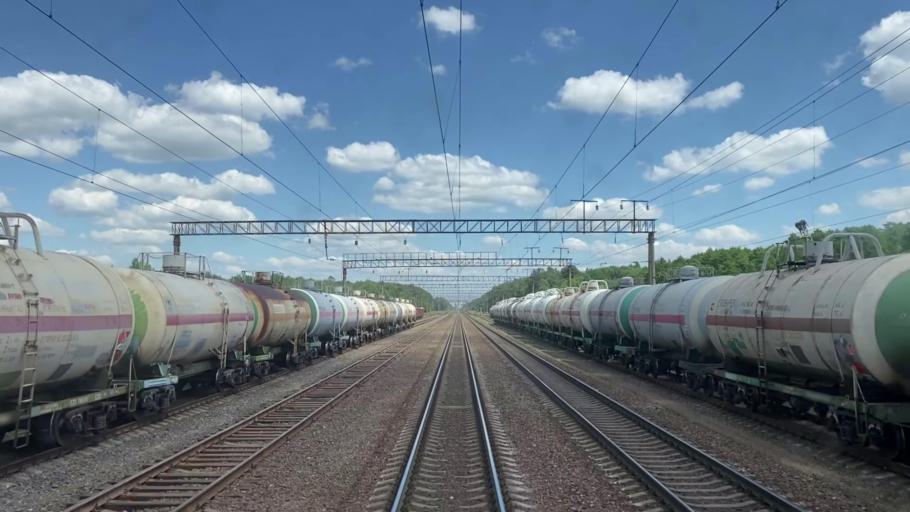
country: BY
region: Brest
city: Pruzhany
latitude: 52.4756
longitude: 24.5394
